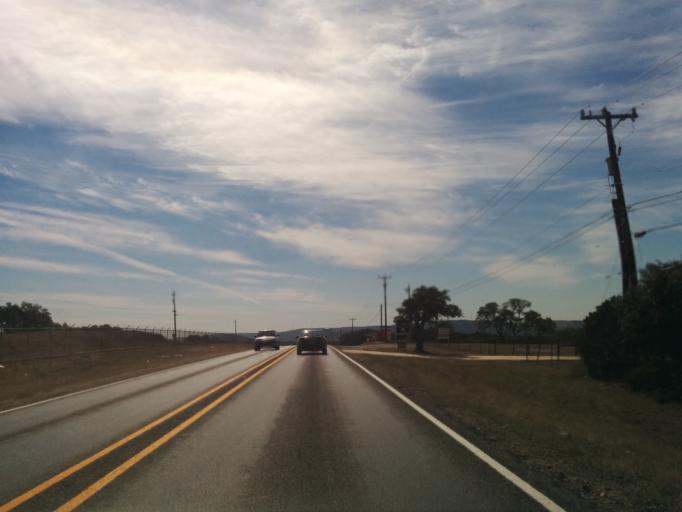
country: US
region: Texas
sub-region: Bexar County
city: Scenic Oaks
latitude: 29.6917
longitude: -98.6315
